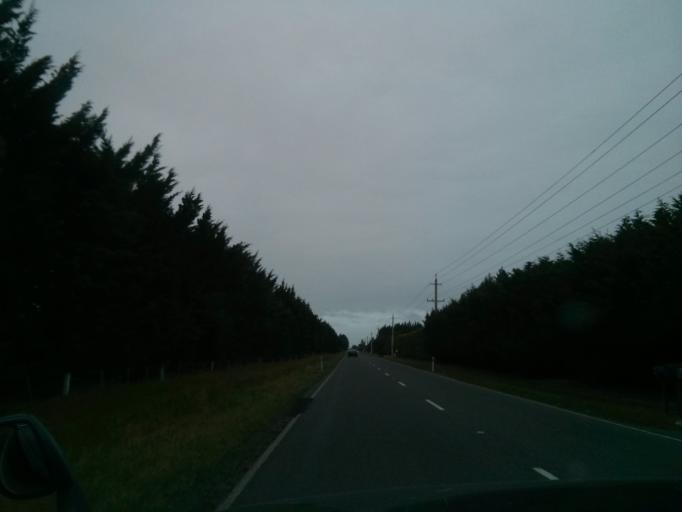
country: NZ
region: Canterbury
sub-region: Waimakariri District
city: Kaiapoi
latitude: -43.3773
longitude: 172.5273
